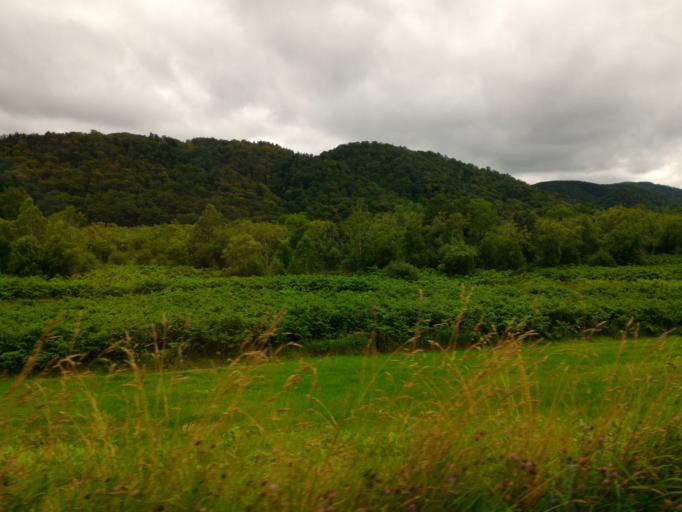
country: JP
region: Hokkaido
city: Nayoro
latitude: 44.7909
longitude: 142.0650
